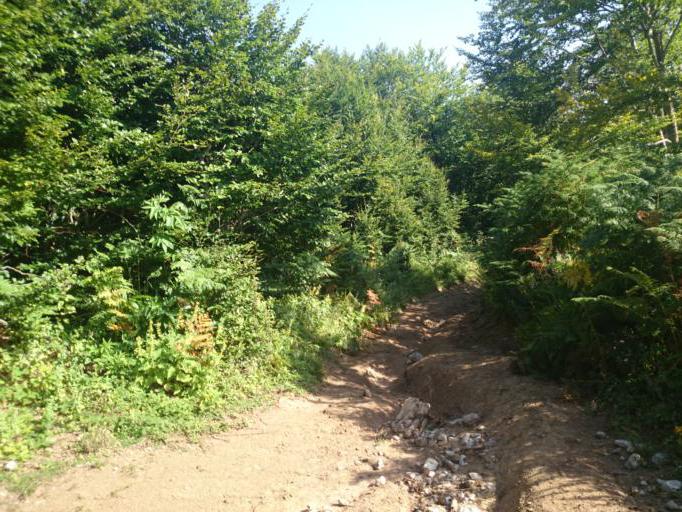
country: AL
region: Elbasan
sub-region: Rrethi i Librazhdit
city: Orenje
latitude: 41.3110
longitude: 20.1558
